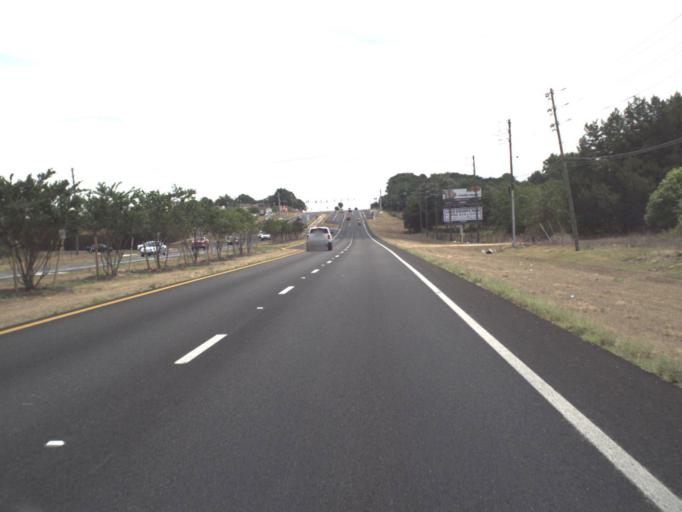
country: US
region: Florida
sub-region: Lake County
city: Groveland
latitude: 28.5579
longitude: -81.8280
